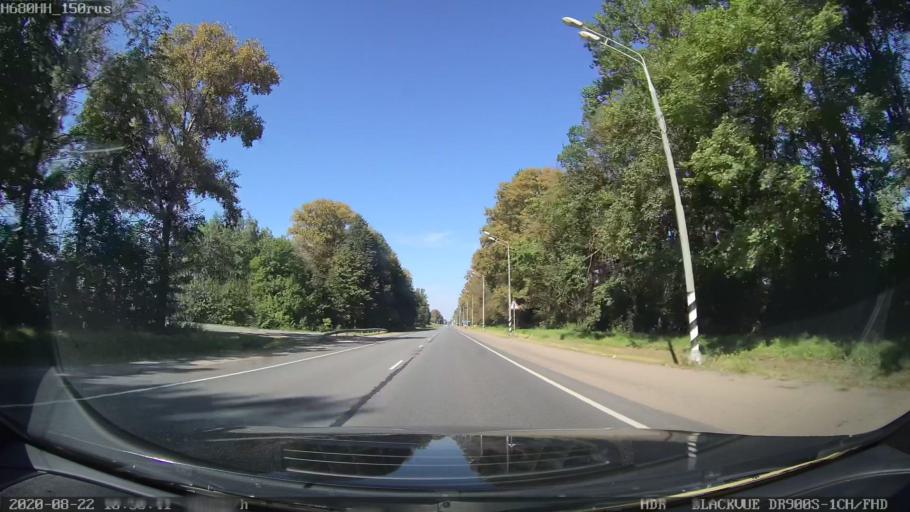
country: RU
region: Tverskaya
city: Emmaus
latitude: 56.7839
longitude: 36.0952
